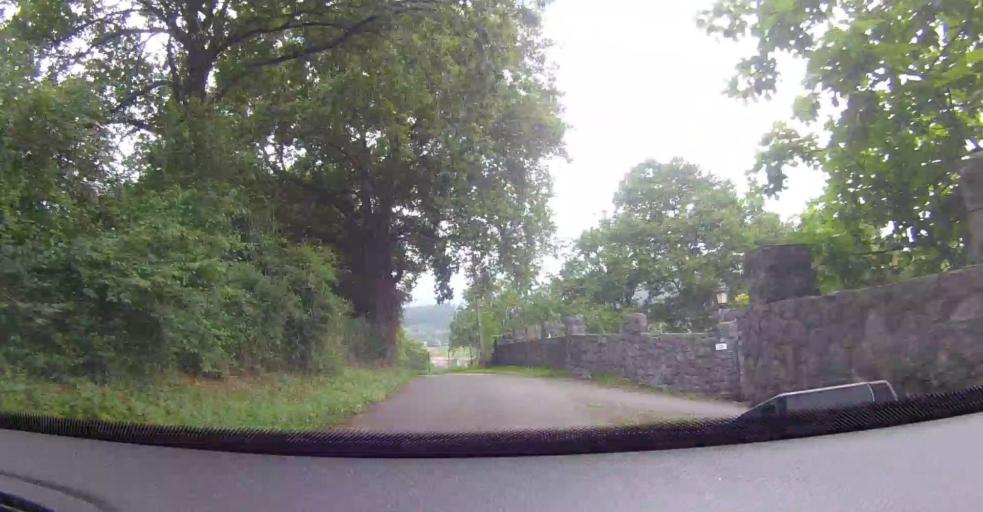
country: ES
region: Basque Country
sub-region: Bizkaia
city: Sopuerta
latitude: 43.2593
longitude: -3.1484
